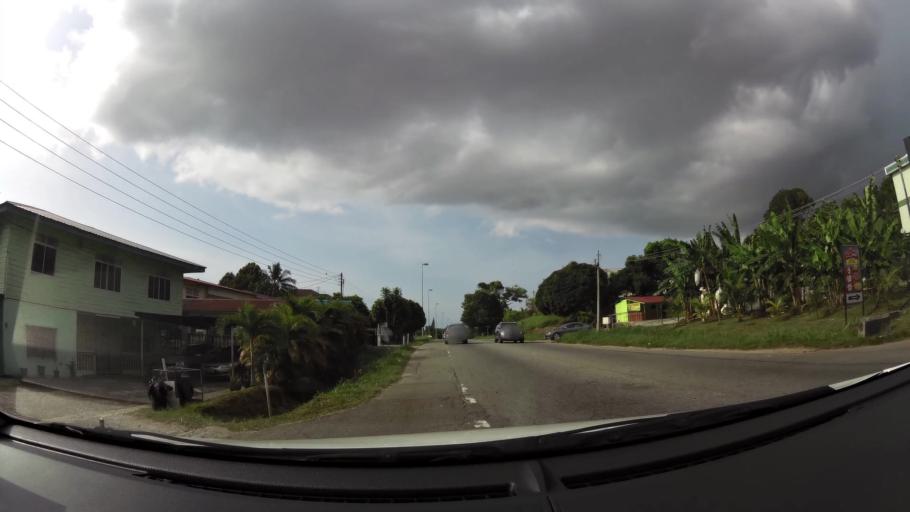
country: BN
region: Brunei and Muara
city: Bandar Seri Begawan
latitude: 4.9599
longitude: 114.9744
